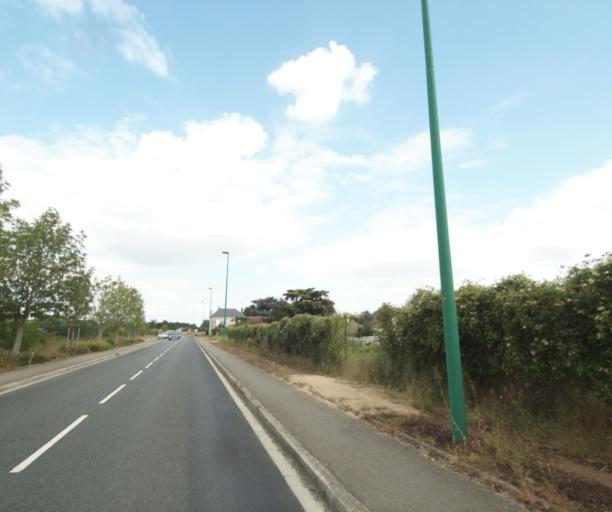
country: FR
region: Centre
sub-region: Departement du Loiret
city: Saint-Pryve-Saint-Mesmin
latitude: 47.8926
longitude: 1.8722
